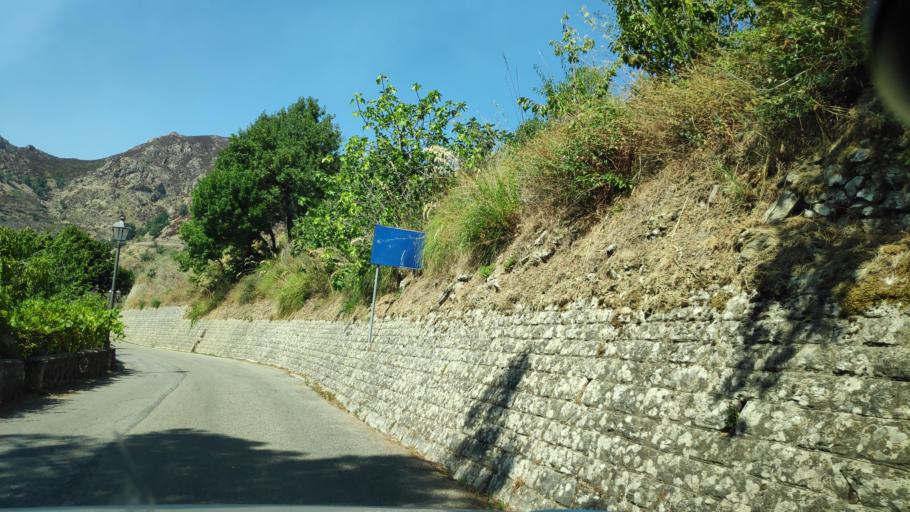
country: IT
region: Calabria
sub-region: Provincia di Reggio Calabria
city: Bova
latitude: 37.9945
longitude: 15.9295
